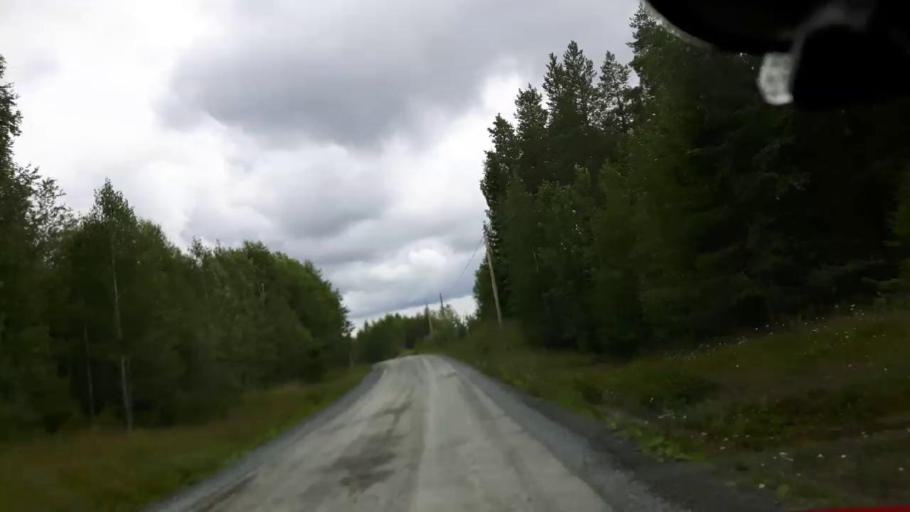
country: SE
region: Jaemtland
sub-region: Krokoms Kommun
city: Krokom
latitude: 63.5806
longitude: 14.1963
